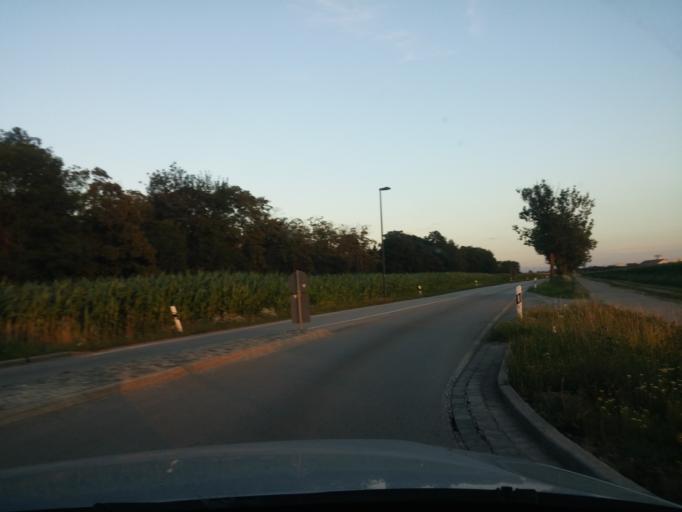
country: DE
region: Bavaria
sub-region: Upper Bavaria
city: Kirchheim bei Muenchen
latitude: 48.1601
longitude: 11.7842
